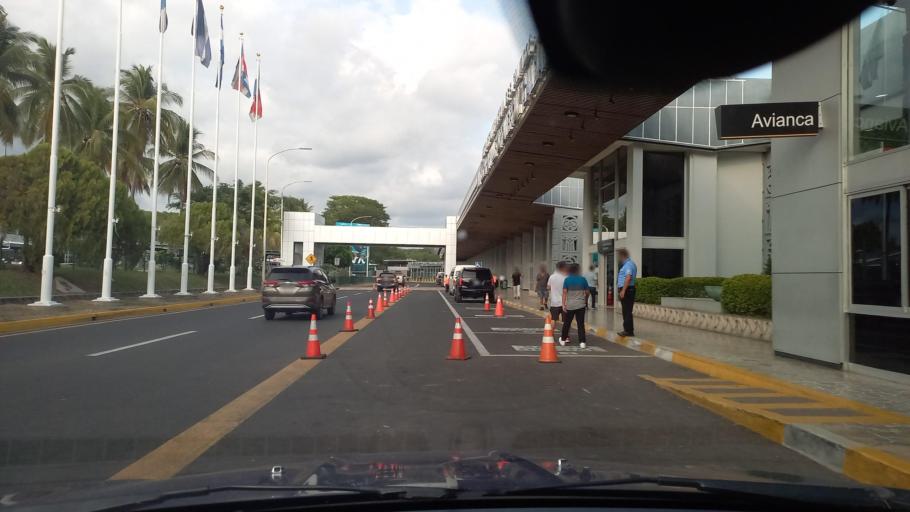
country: SV
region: La Paz
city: El Rosario
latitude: 13.4452
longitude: -89.0578
